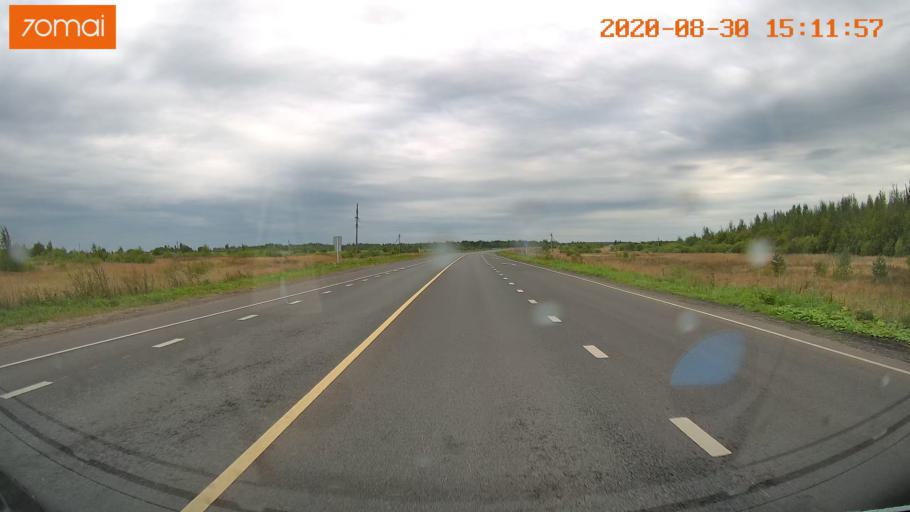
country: RU
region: Ivanovo
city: Vichuga
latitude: 57.1980
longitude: 41.8770
